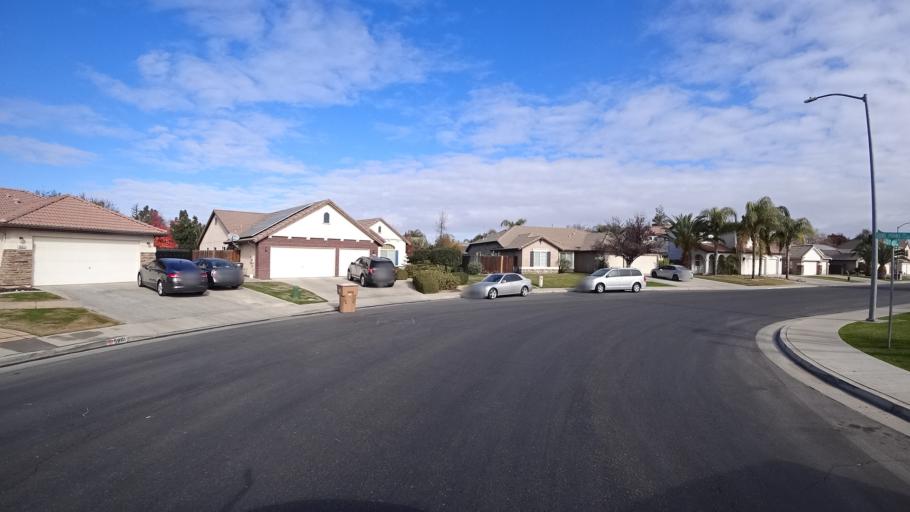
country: US
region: California
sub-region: Kern County
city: Greenacres
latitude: 35.3019
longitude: -119.1274
